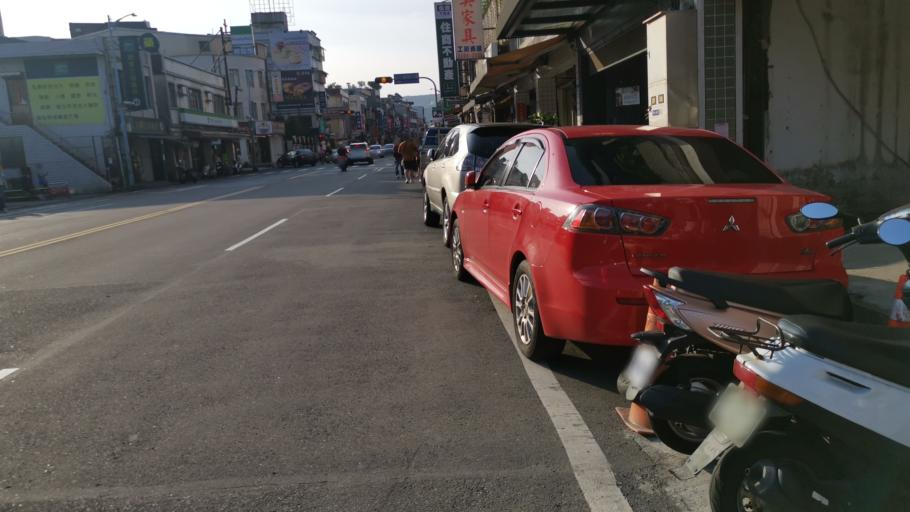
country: TW
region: Taiwan
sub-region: Keelung
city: Keelung
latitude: 25.2189
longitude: 121.6402
